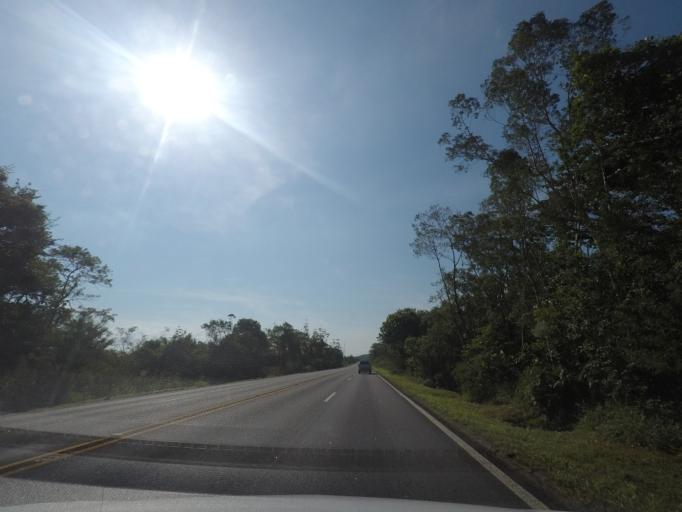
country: BR
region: Parana
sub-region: Paranagua
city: Paranagua
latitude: -25.5879
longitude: -48.6115
